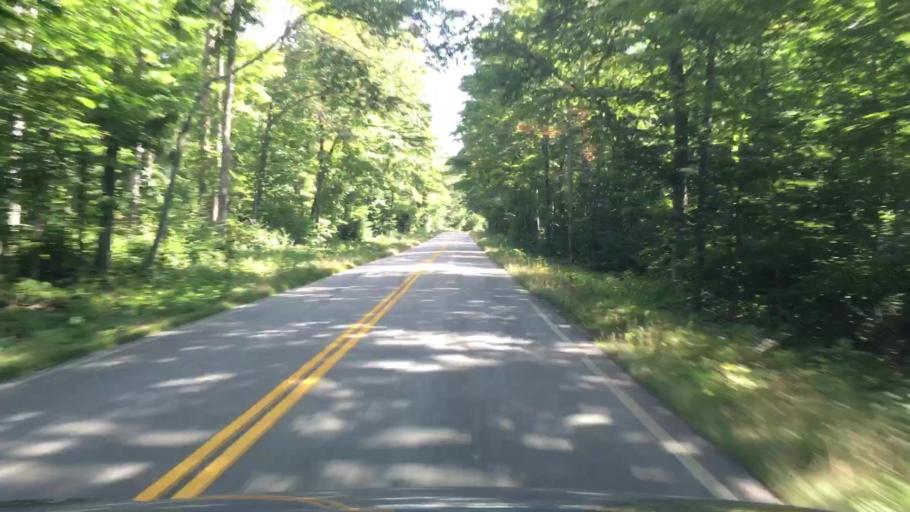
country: US
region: New Hampshire
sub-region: Carroll County
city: Tamworth
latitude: 44.0197
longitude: -71.3204
